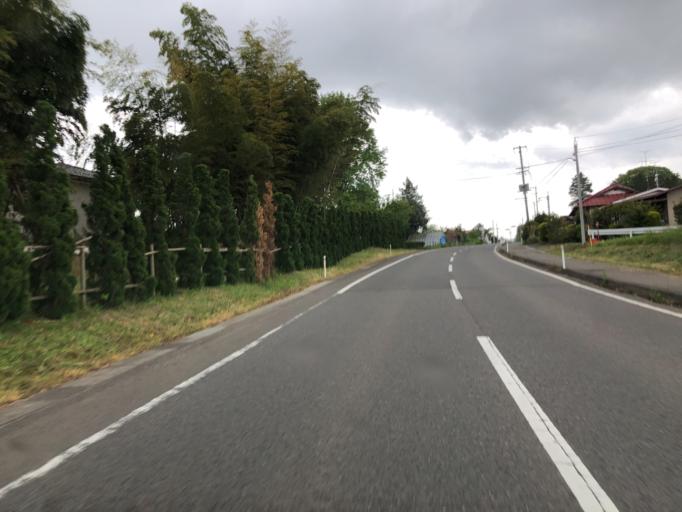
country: JP
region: Fukushima
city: Ishikawa
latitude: 37.1506
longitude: 140.3661
